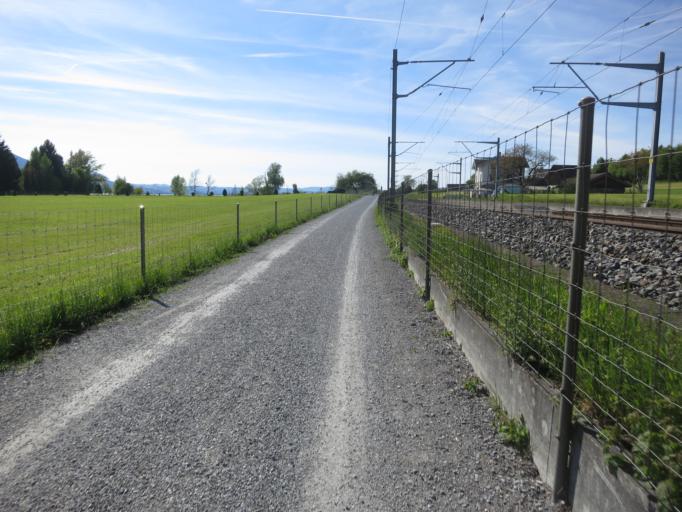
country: CH
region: Schwyz
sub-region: Bezirk March
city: Lachen
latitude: 47.2169
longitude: 8.8807
